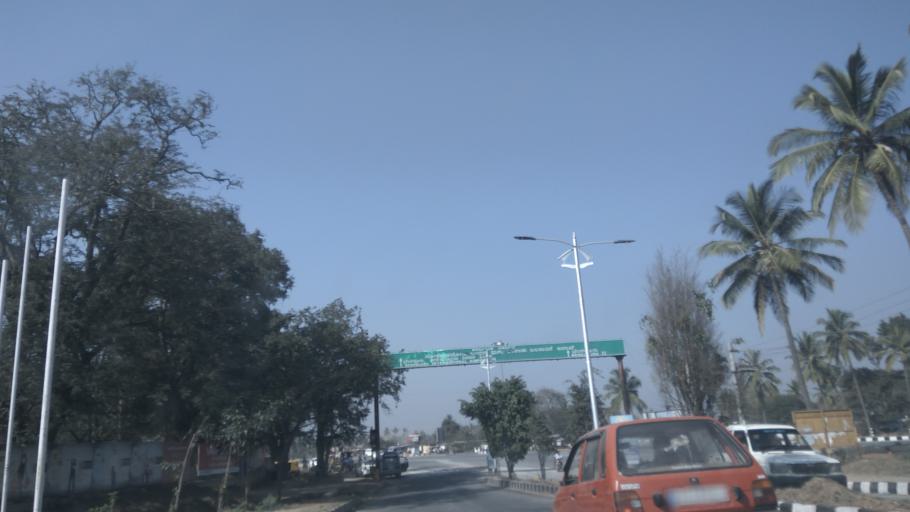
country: IN
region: Karnataka
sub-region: Bangalore Rural
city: Devanhalli
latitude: 13.2427
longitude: 77.7052
